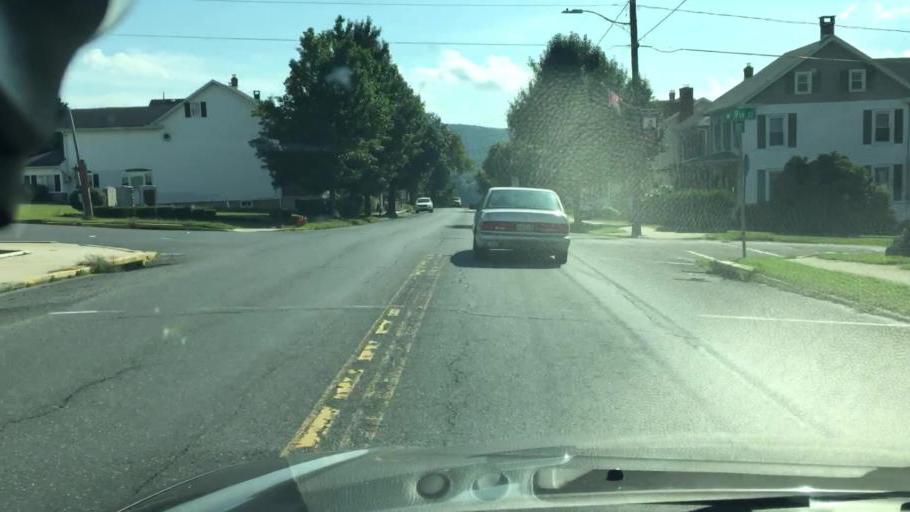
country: US
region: Pennsylvania
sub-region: Carbon County
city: Jim Thorpe
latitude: 40.8788
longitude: -75.7291
